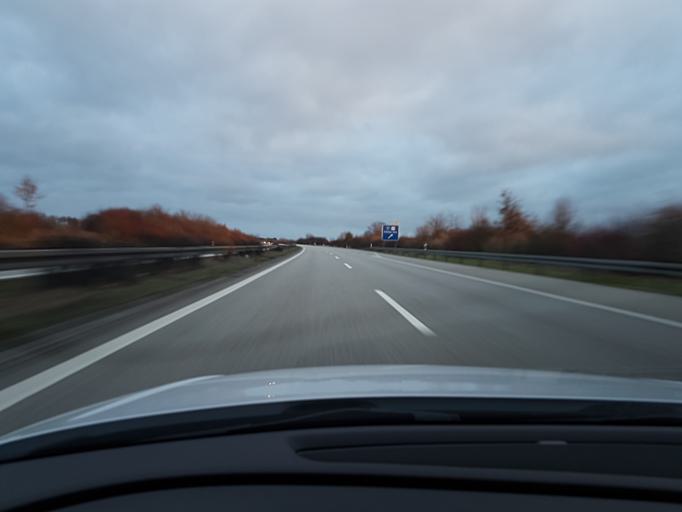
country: DE
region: Mecklenburg-Vorpommern
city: Grevesmuhlen
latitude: 53.8272
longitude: 11.2449
